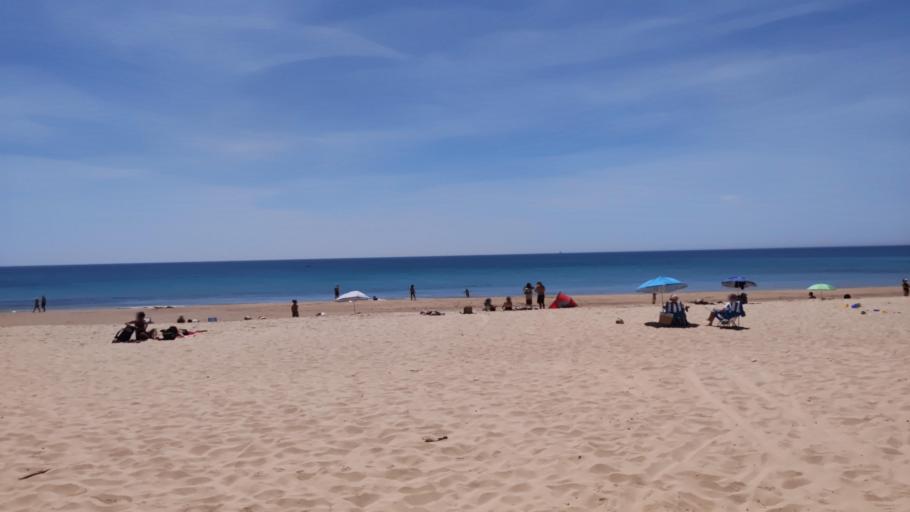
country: PT
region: Faro
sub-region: Lagos
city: Lagos
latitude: 37.0718
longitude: -8.7757
